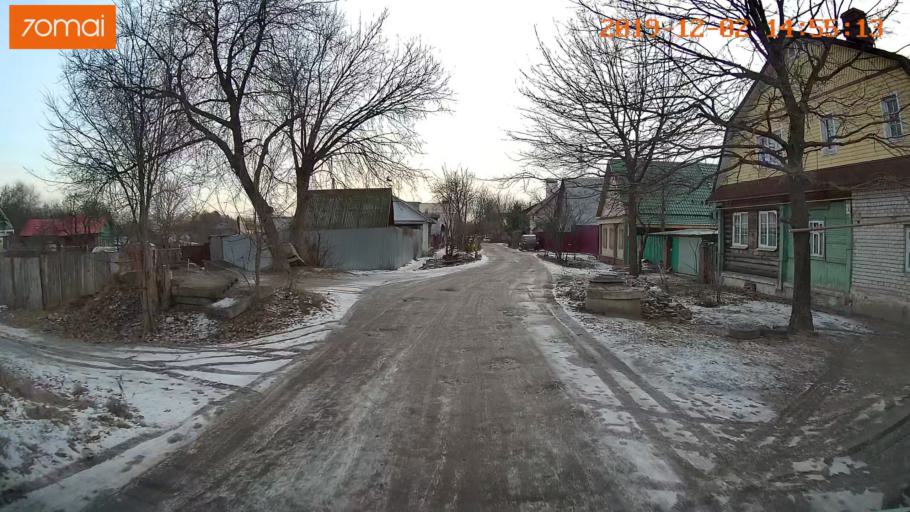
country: RU
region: Ivanovo
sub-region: Gorod Ivanovo
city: Ivanovo
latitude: 56.9736
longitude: 41.0175
